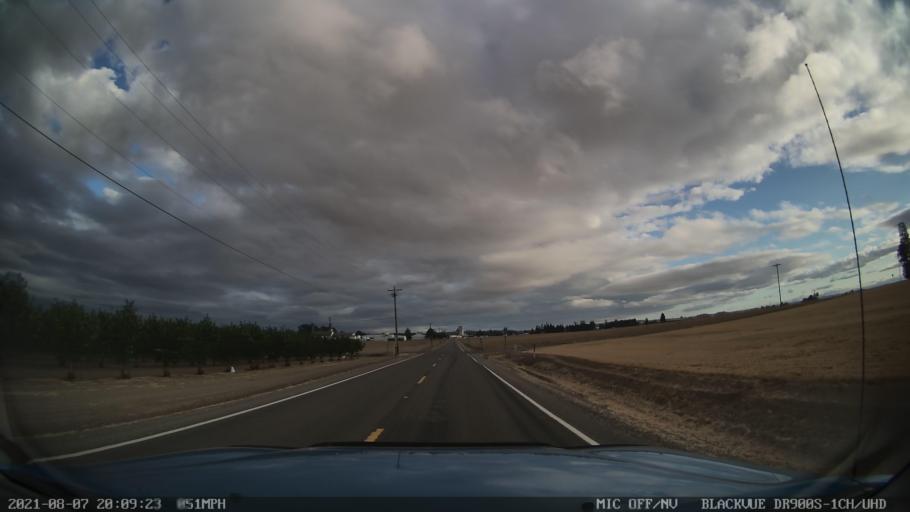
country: US
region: Oregon
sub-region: Marion County
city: Silverton
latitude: 44.9718
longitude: -122.8774
